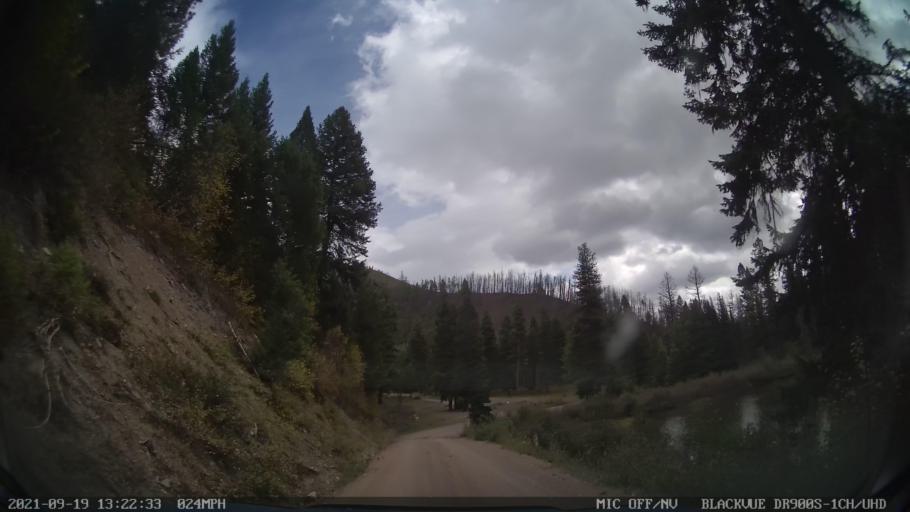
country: US
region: Montana
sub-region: Missoula County
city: Seeley Lake
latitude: 47.1638
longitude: -113.3481
